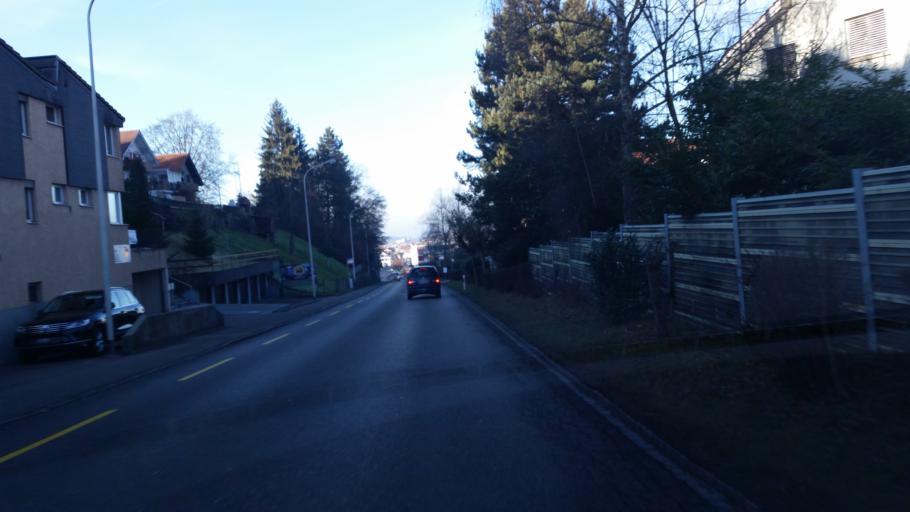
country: CH
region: Saint Gallen
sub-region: Wahlkreis St. Gallen
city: Gossau
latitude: 47.4074
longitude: 9.2530
